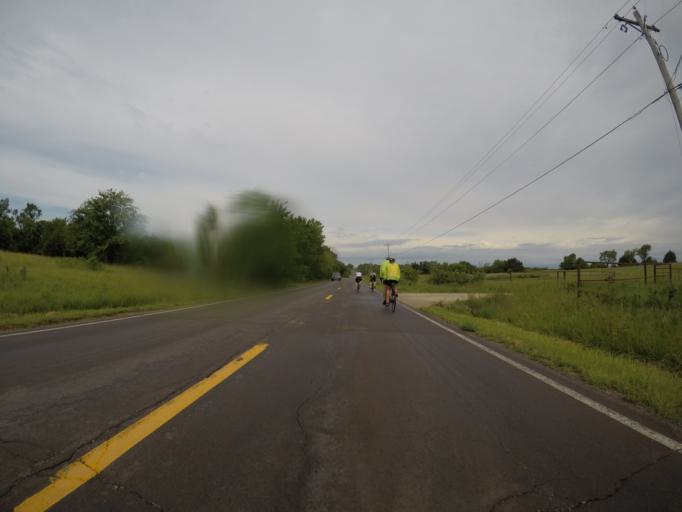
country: US
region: Kansas
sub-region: Shawnee County
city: Auburn
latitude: 38.9564
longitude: -95.7745
